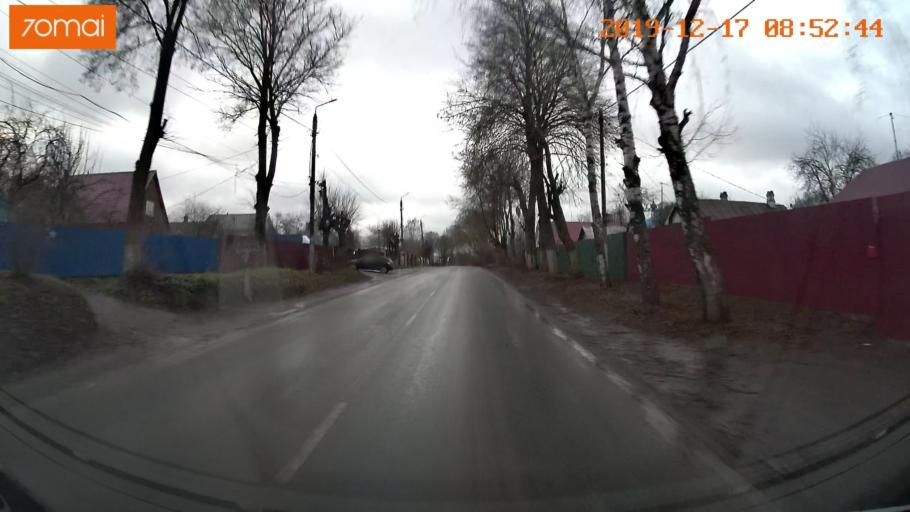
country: RU
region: Vladimir
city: Kosterevo
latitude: 55.9461
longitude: 39.6320
